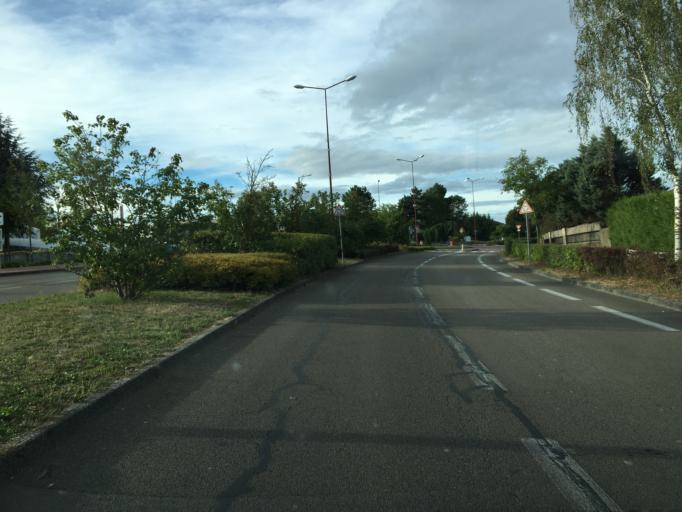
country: FR
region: Bourgogne
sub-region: Departement de la Cote-d'Or
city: Daix
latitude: 47.3404
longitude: 4.9971
